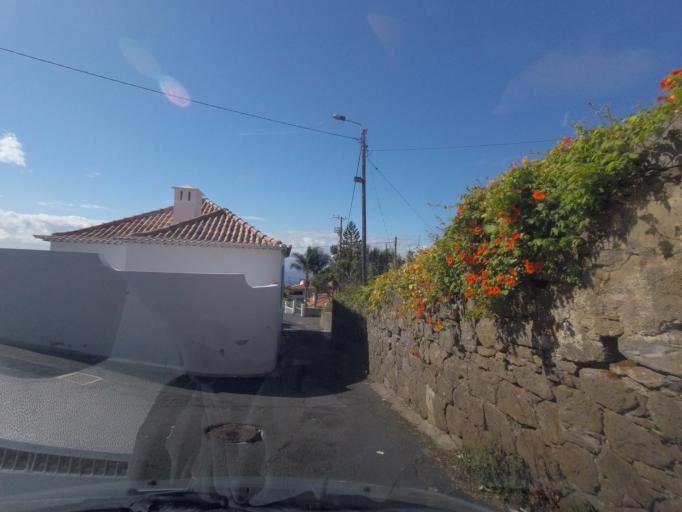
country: PT
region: Madeira
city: Camara de Lobos
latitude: 32.6646
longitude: -16.9754
